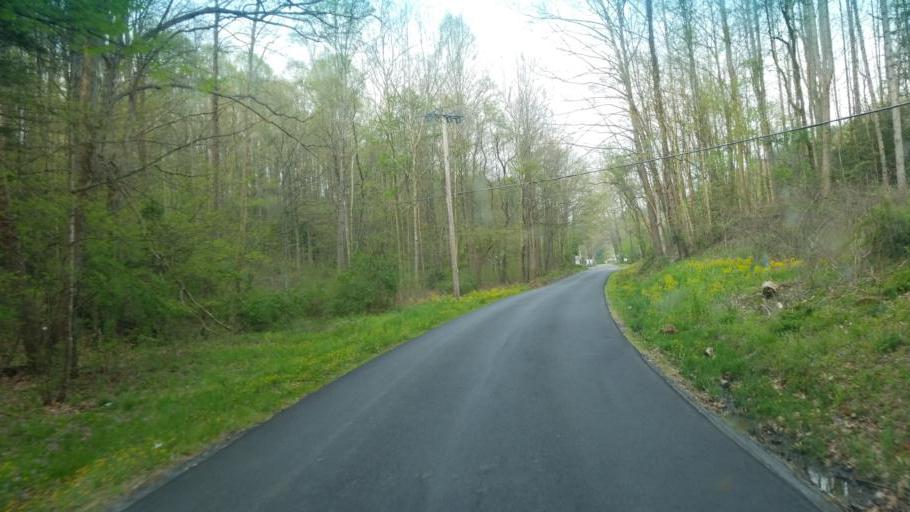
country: US
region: Virginia
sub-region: Smyth County
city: Marion
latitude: 36.8101
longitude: -81.4650
